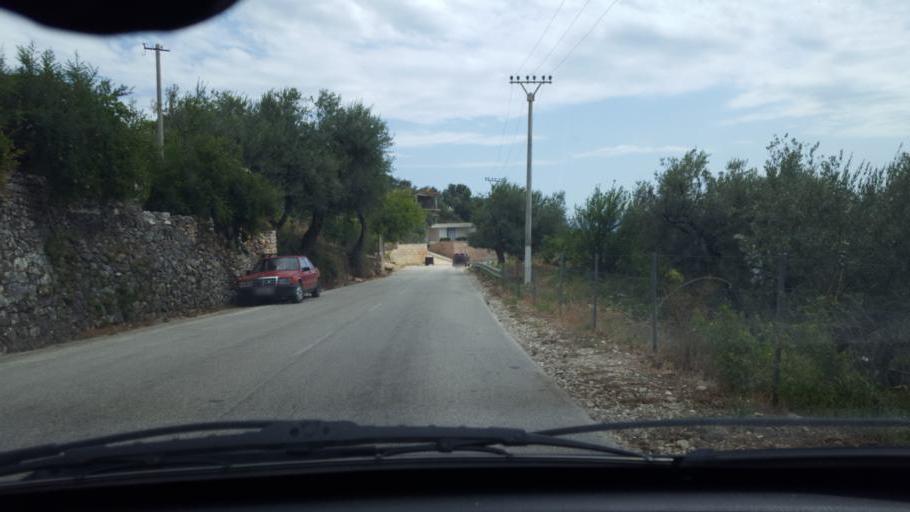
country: AL
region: Vlore
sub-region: Rrethi i Sarandes
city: Lukove
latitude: 39.9901
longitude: 19.9152
